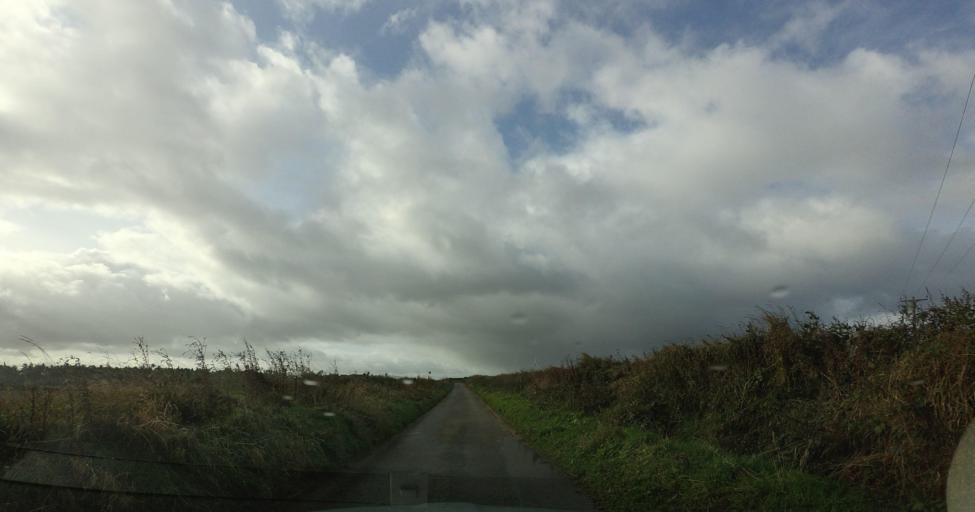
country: GB
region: Scotland
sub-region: Aberdeenshire
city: Whitehills
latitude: 57.6689
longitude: -2.5908
